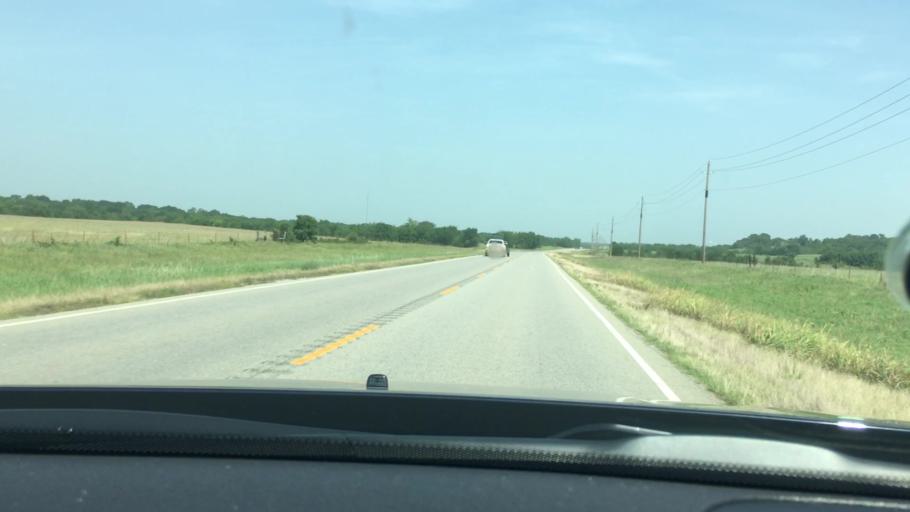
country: US
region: Oklahoma
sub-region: Atoka County
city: Atoka
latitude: 34.4335
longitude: -96.1993
